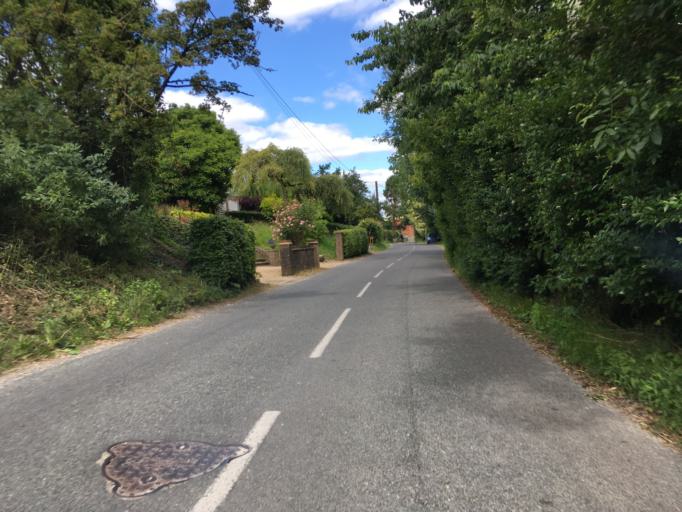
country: GB
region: England
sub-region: Hampshire
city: Andover
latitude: 51.2633
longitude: -1.4229
